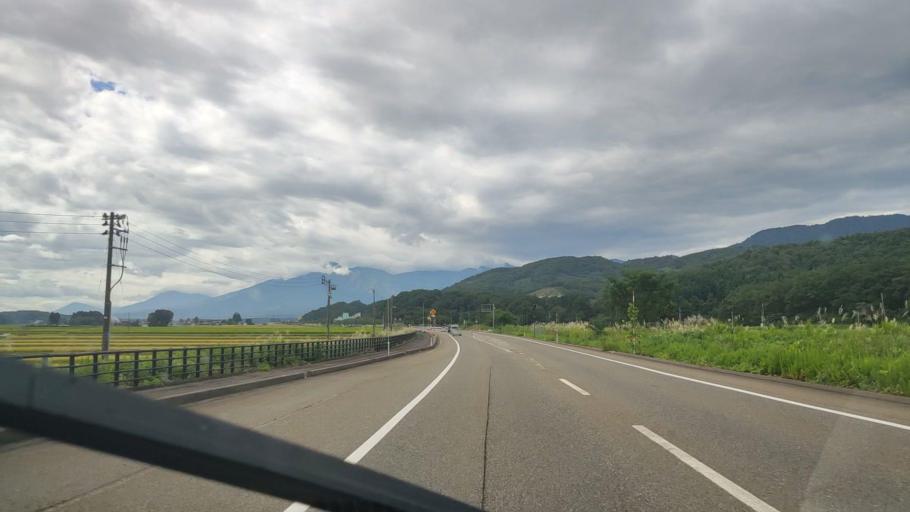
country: JP
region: Niigata
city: Arai
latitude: 37.0474
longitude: 138.2420
